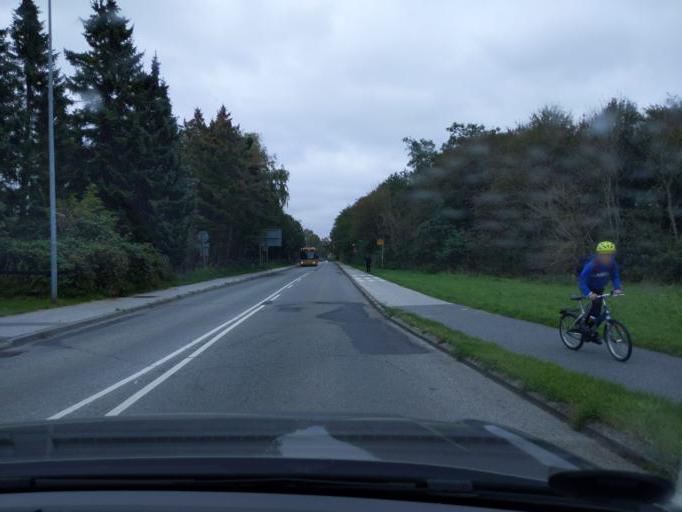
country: DK
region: Central Jutland
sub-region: Randers Kommune
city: Randers
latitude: 56.4611
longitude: 9.9644
